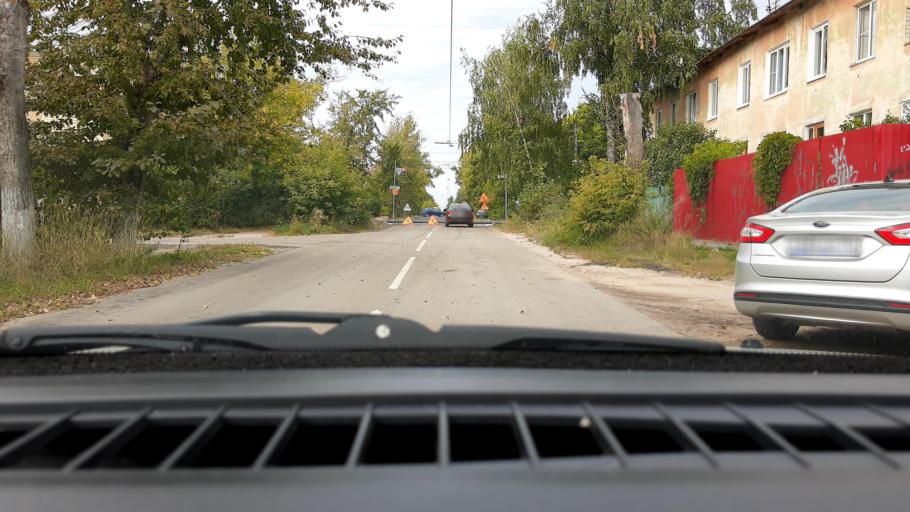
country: RU
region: Nizjnij Novgorod
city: Dzerzhinsk
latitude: 56.2500
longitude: 43.4744
